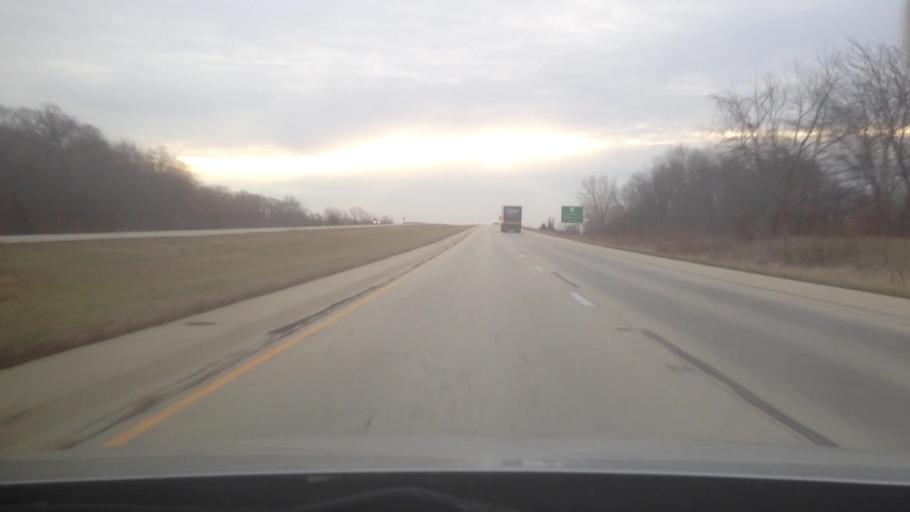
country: US
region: Illinois
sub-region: Macon County
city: Decatur
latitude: 39.8049
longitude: -89.0160
